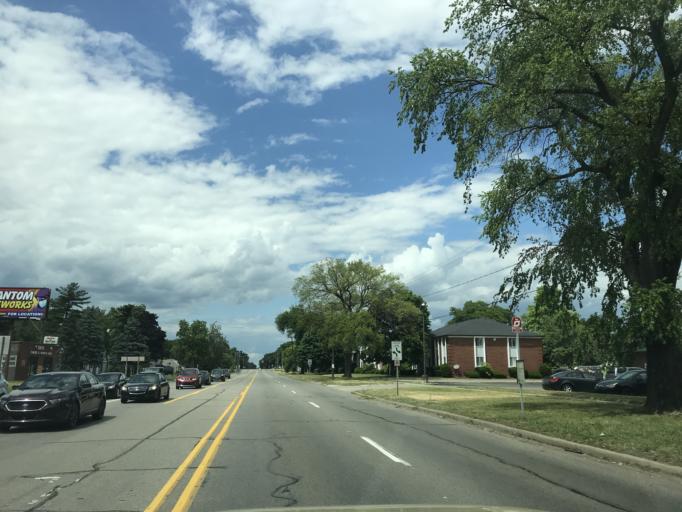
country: US
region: Michigan
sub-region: Wayne County
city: Garden City
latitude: 42.3513
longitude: -83.3126
